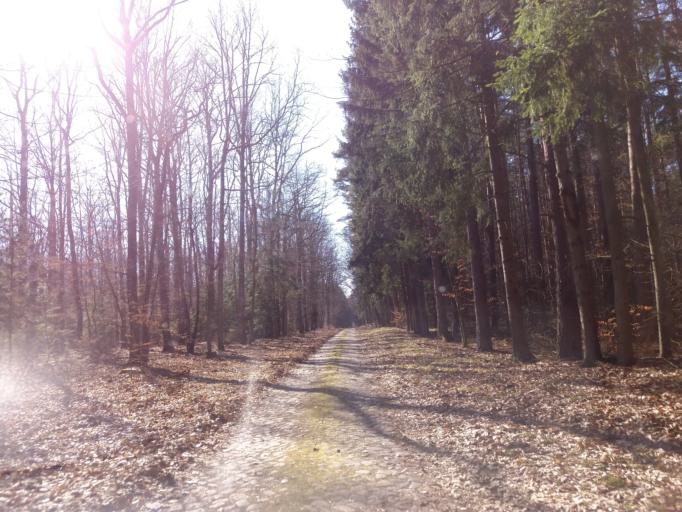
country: PL
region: West Pomeranian Voivodeship
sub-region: Powiat choszczenski
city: Drawno
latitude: 53.1065
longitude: 15.8859
